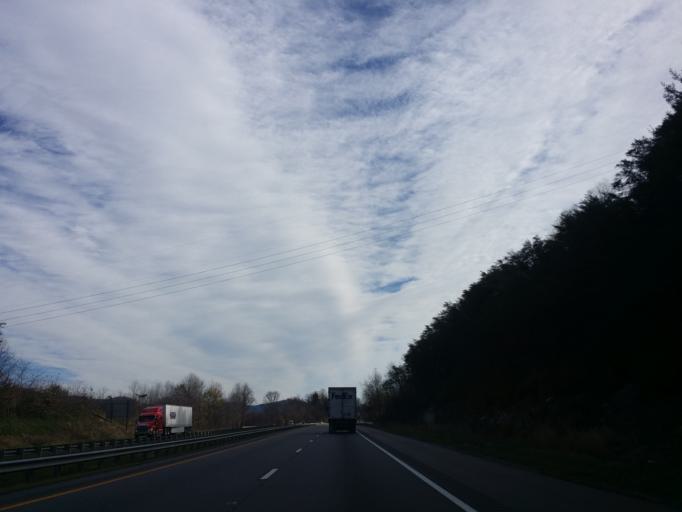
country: US
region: North Carolina
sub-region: Buncombe County
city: Swannanoa
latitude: 35.5968
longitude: -82.3950
